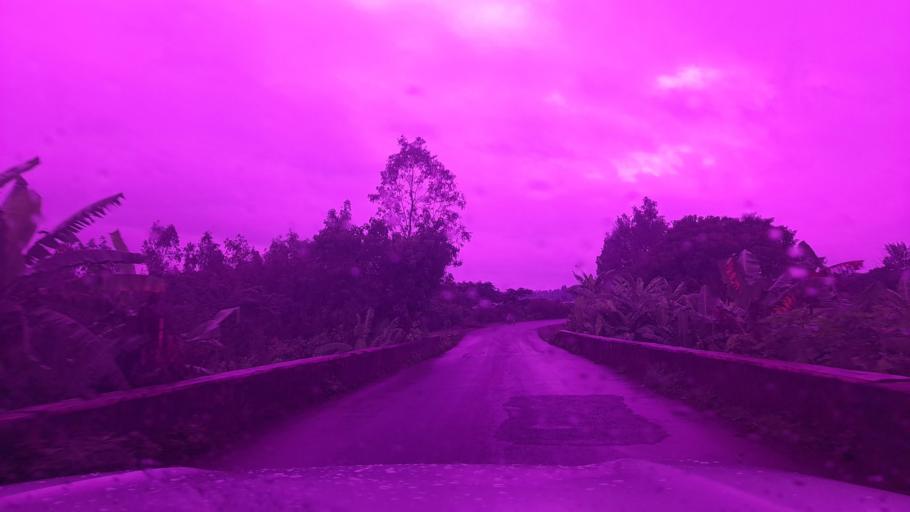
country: ET
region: Oromiya
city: Jima
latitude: 7.8250
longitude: 37.3455
